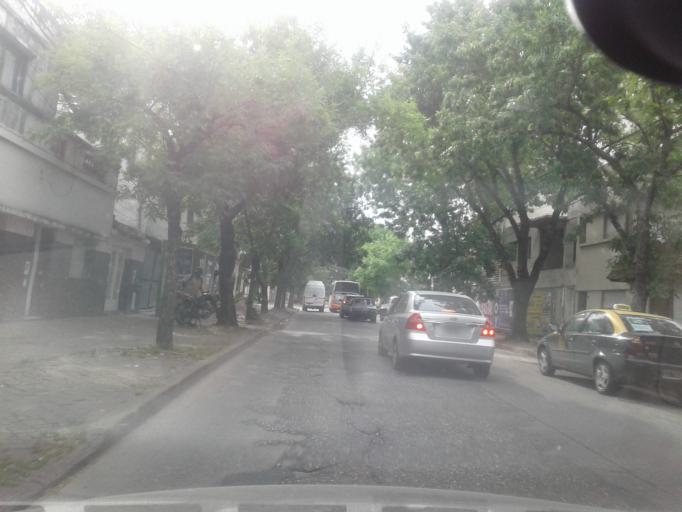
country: AR
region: Santa Fe
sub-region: Departamento de Rosario
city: Rosario
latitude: -32.9672
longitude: -60.6527
